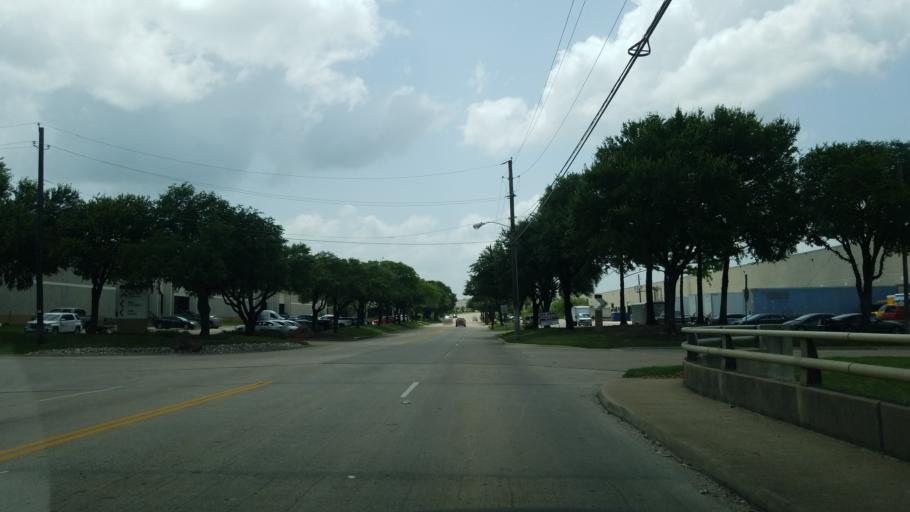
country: US
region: Texas
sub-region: Dallas County
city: Cockrell Hill
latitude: 32.7711
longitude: -96.8913
